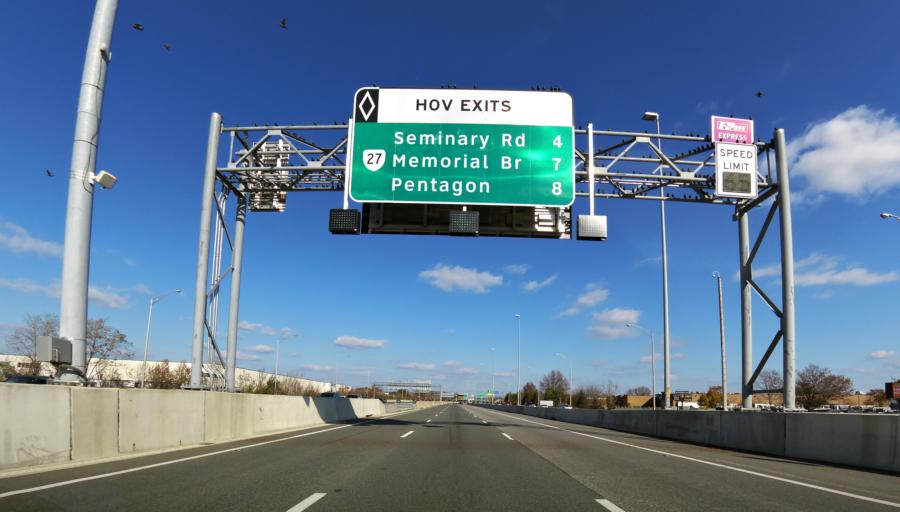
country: US
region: Virginia
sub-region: Fairfax County
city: Springfield
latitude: 38.7961
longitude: -77.1702
